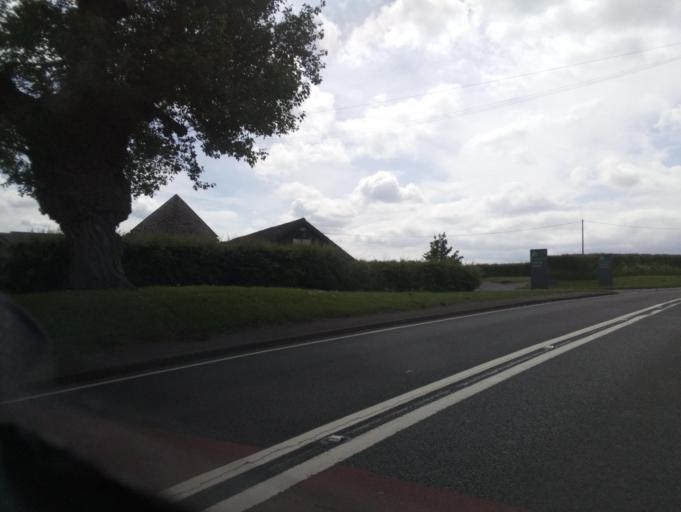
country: GB
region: England
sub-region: Herefordshire
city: Sellack
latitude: 51.9173
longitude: -2.6158
